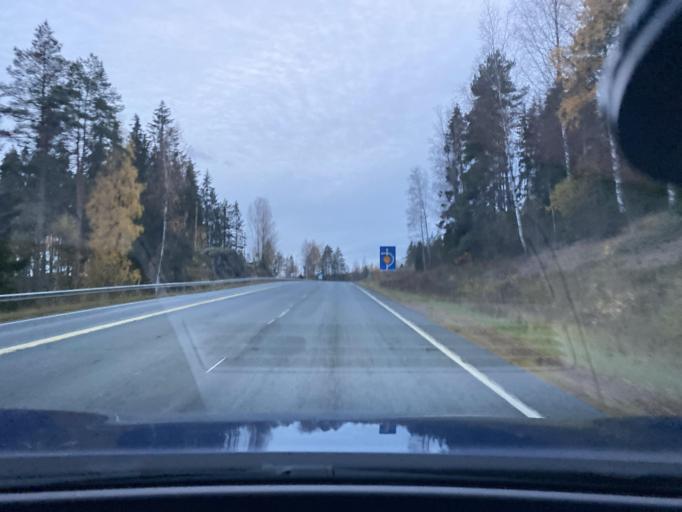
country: FI
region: Uusimaa
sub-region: Helsinki
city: Sammatti
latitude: 60.3836
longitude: 23.7543
